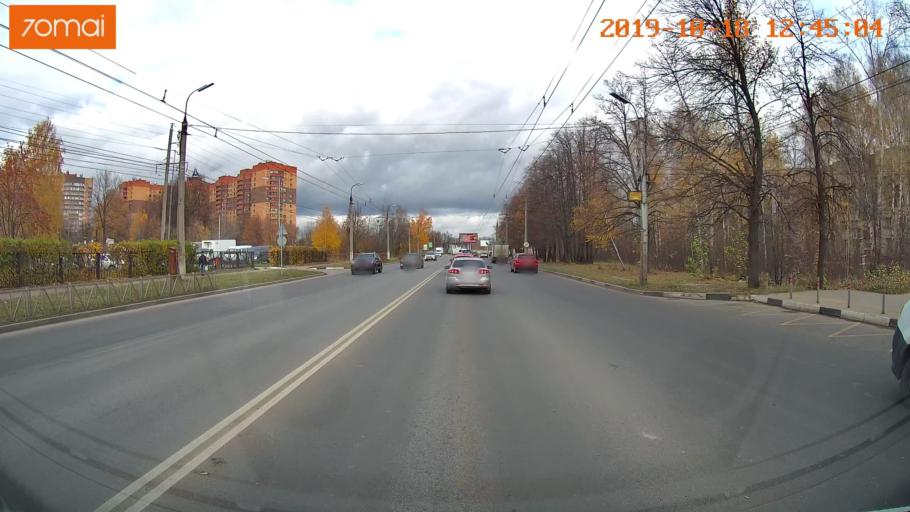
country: RU
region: Rjazan
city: Ryazan'
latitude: 54.6501
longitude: 39.6643
